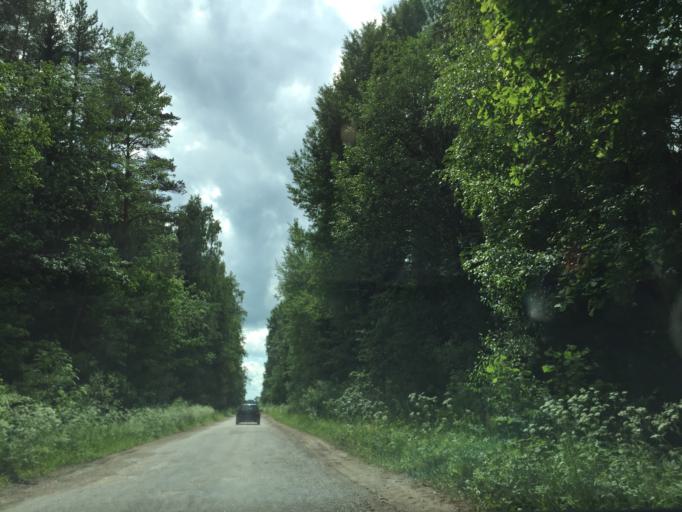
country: LV
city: Tireli
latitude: 56.6998
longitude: 23.4609
